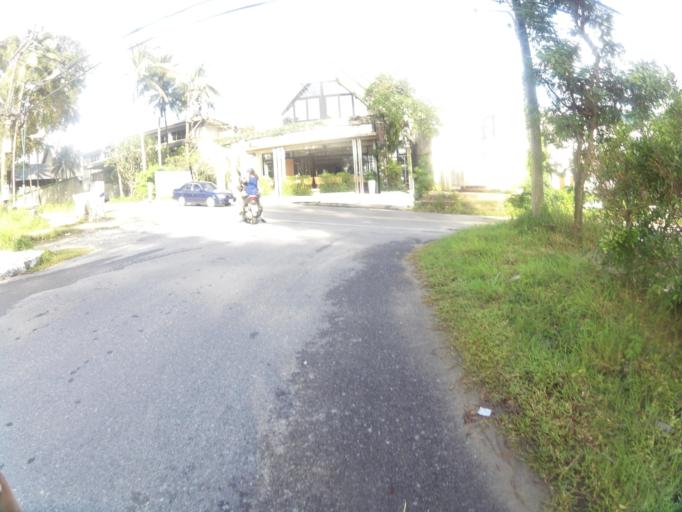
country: TH
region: Phuket
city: Thalang
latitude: 7.9767
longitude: 98.2802
